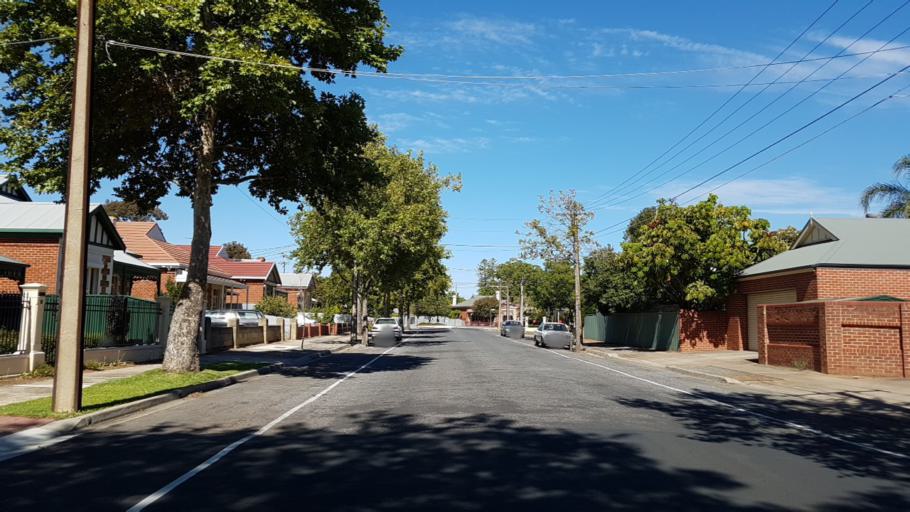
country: AU
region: South Australia
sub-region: City of West Torrens
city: Thebarton
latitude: -34.9200
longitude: 138.5660
